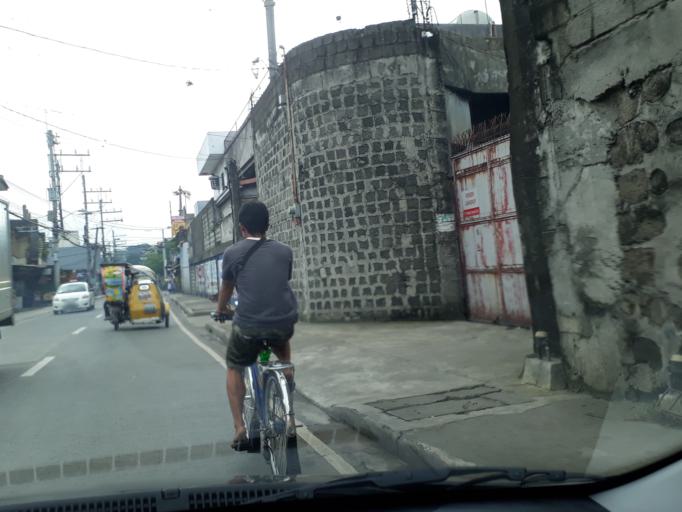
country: PH
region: Calabarzon
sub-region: Province of Rizal
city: Valenzuela
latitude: 14.7150
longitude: 120.9737
